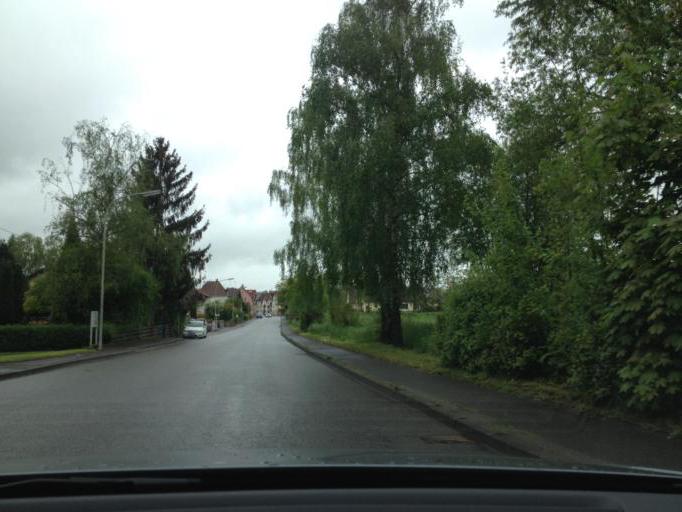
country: DE
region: Baden-Wuerttemberg
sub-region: Regierungsbezirk Stuttgart
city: Untereisesheim
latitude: 49.2298
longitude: 9.1862
